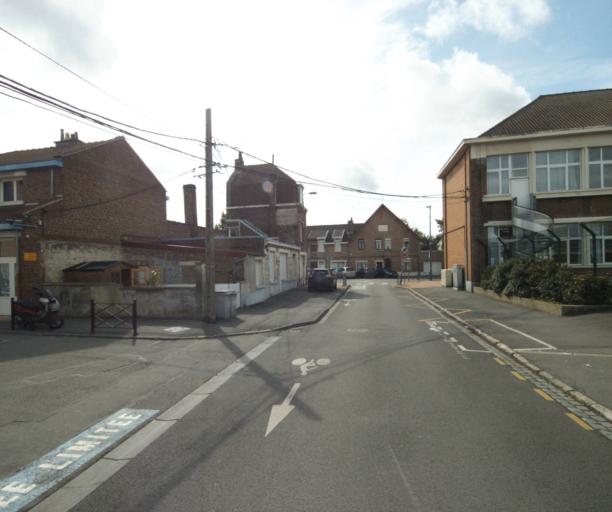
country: FR
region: Nord-Pas-de-Calais
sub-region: Departement du Nord
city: Loos
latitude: 50.6314
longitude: 3.0134
